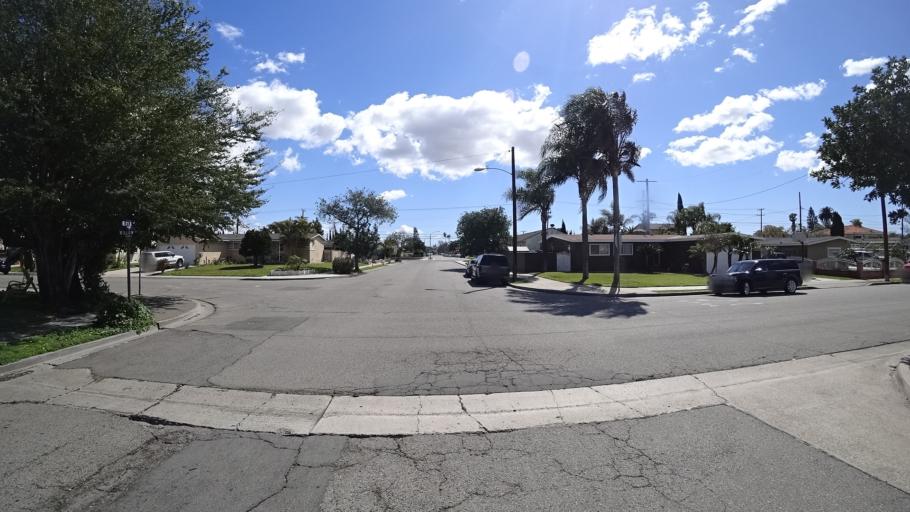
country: US
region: California
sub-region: Orange County
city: Anaheim
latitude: 33.8363
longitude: -117.8942
